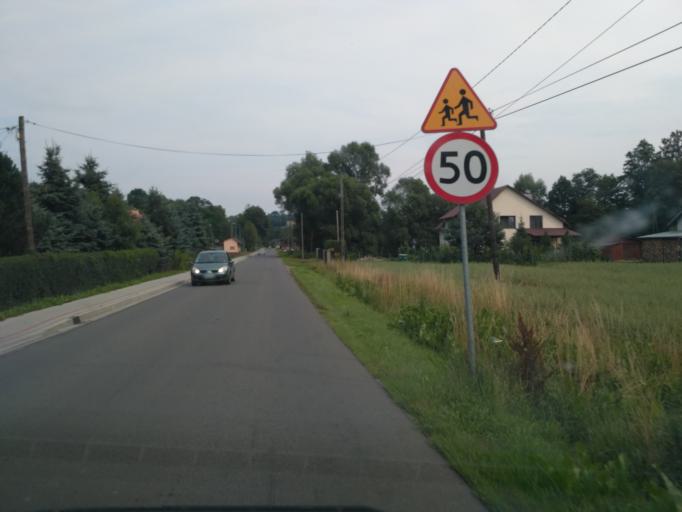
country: PL
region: Subcarpathian Voivodeship
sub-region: Powiat strzyzowski
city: Konieczkowa
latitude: 49.8432
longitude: 21.9229
